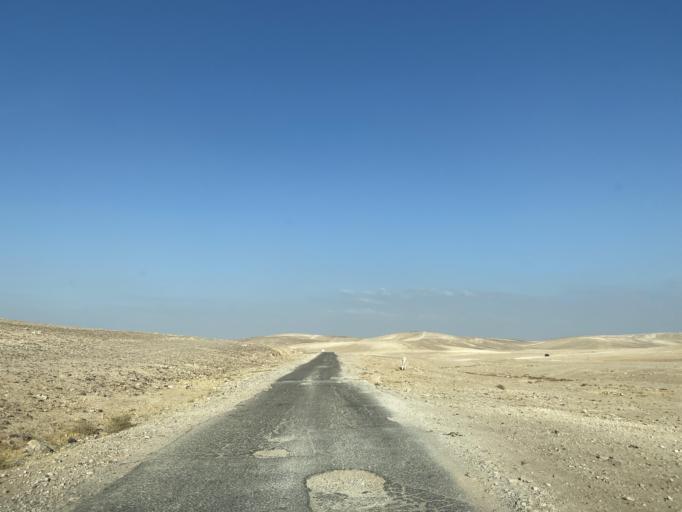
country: PS
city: `Arab ar Rashaydah
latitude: 31.5328
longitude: 35.2809
